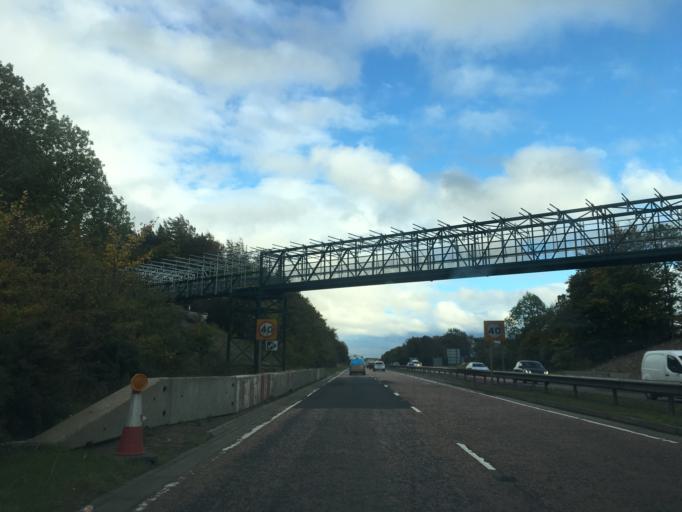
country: GB
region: Scotland
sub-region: Edinburgh
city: Ratho
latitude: 55.9719
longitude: -3.3294
